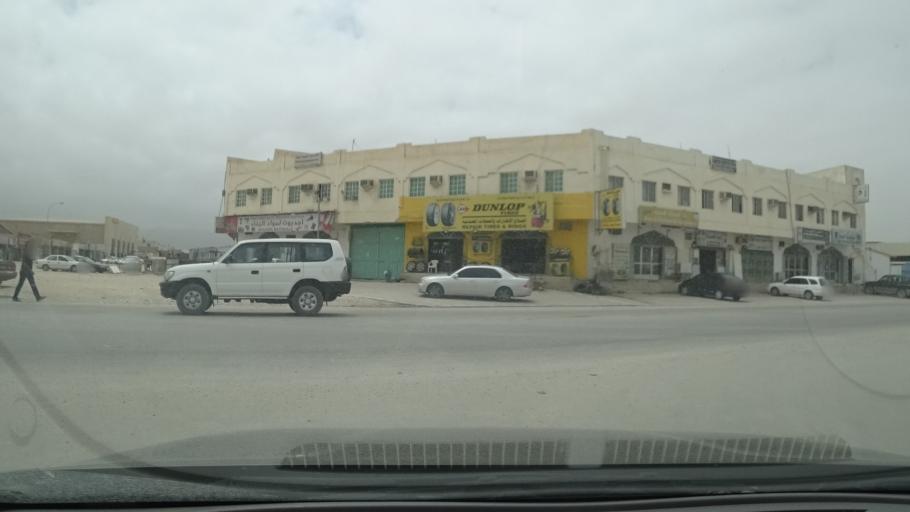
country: OM
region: Zufar
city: Salalah
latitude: 17.0222
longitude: 54.0483
